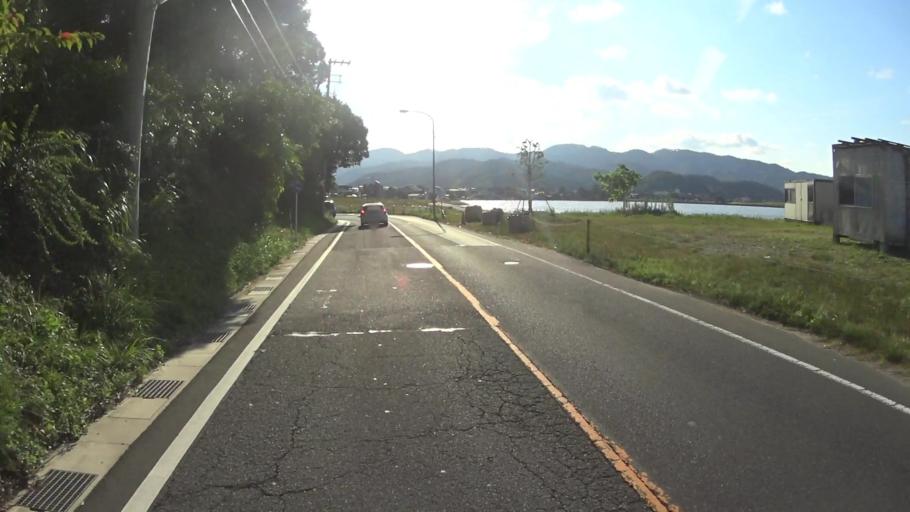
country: JP
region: Hyogo
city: Toyooka
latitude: 35.6067
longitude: 134.9049
